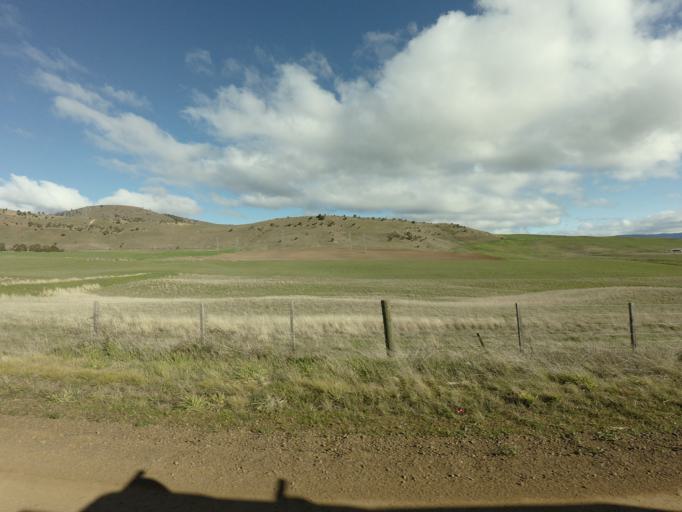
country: AU
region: Tasmania
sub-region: Derwent Valley
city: New Norfolk
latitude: -42.6954
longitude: 146.9703
